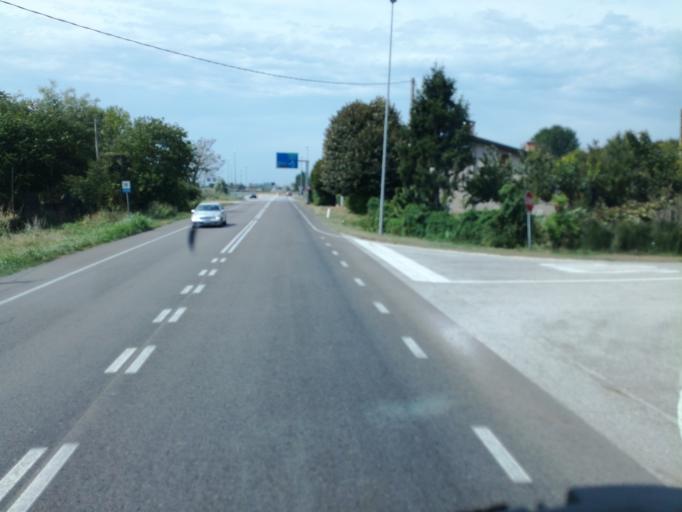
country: IT
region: Veneto
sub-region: Provincia di Padova
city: Arre
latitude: 45.2122
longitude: 11.9066
